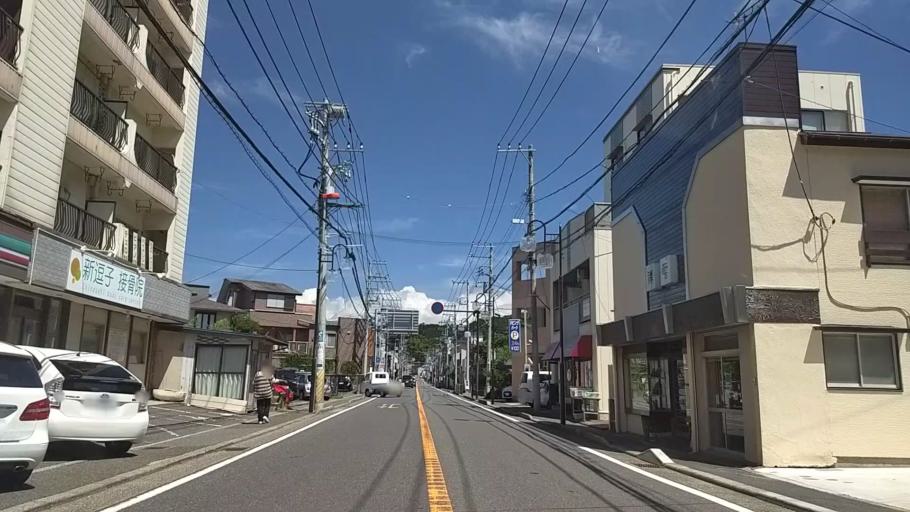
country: JP
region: Kanagawa
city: Zushi
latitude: 35.2957
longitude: 139.5832
